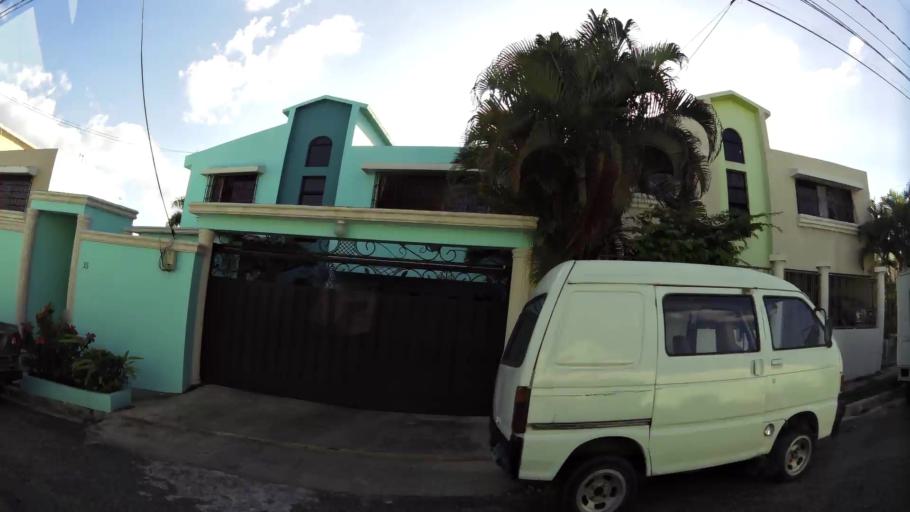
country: DO
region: Nacional
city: Santo Domingo
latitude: 18.4939
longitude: -69.9691
